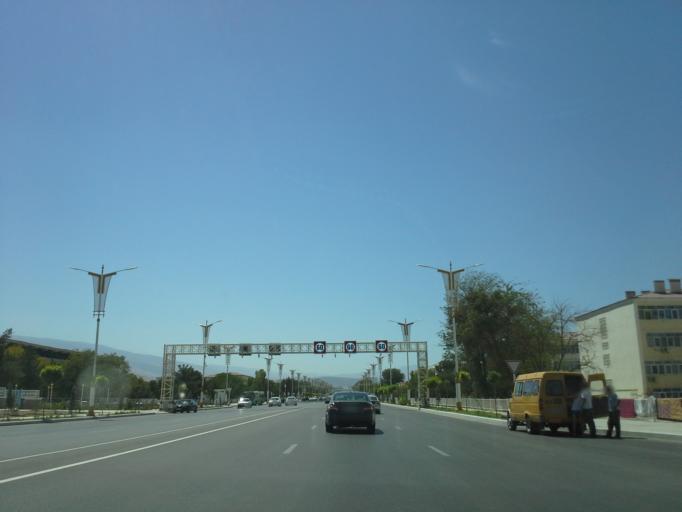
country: TM
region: Ahal
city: Ashgabat
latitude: 37.9101
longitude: 58.4202
